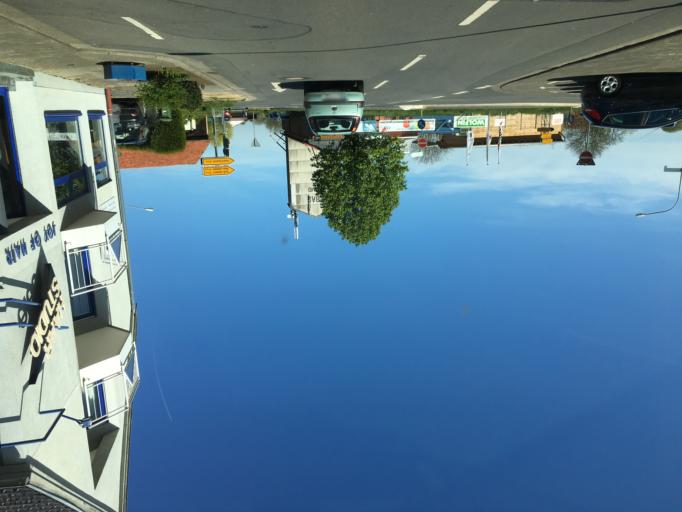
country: DE
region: Hesse
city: Dieburg
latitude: 49.8740
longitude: 8.8834
